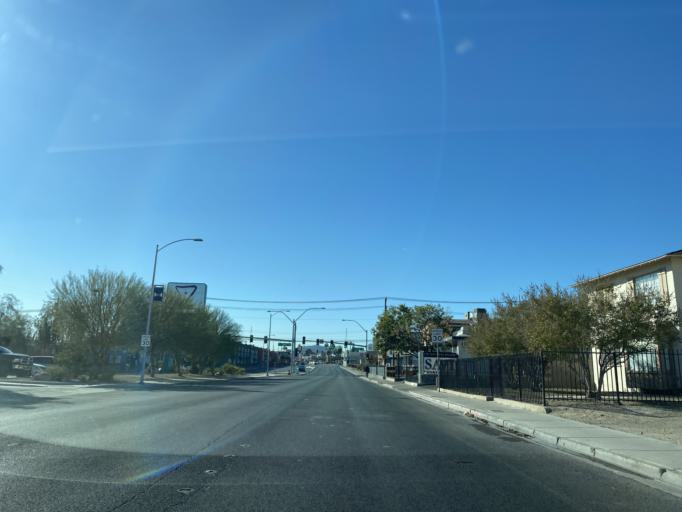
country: US
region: Nevada
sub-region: Clark County
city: Las Vegas
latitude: 36.1620
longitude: -115.1351
